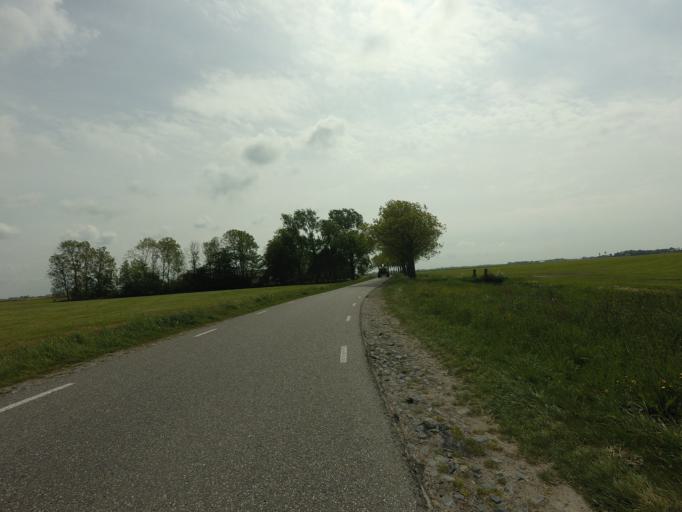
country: NL
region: Friesland
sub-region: Sudwest Fryslan
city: Bolsward
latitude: 53.1104
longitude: 5.4913
